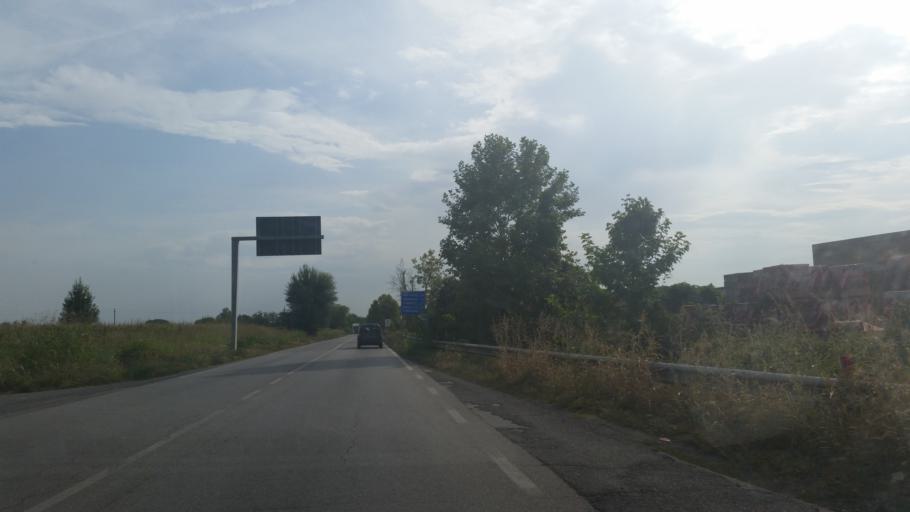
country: IT
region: Lombardy
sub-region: Provincia di Brescia
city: Barbariga
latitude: 45.3777
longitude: 10.0560
